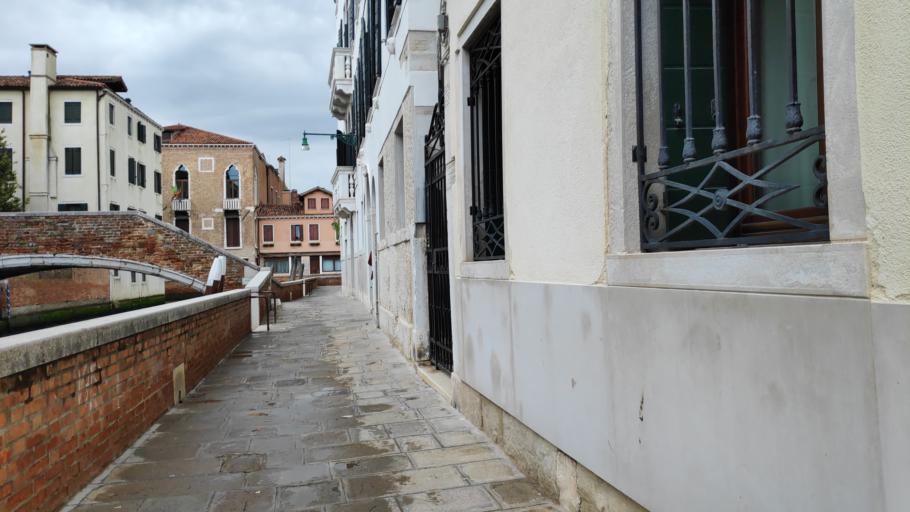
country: IT
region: Veneto
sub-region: Provincia di Venezia
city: Giudecca
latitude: 45.4326
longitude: 12.3201
